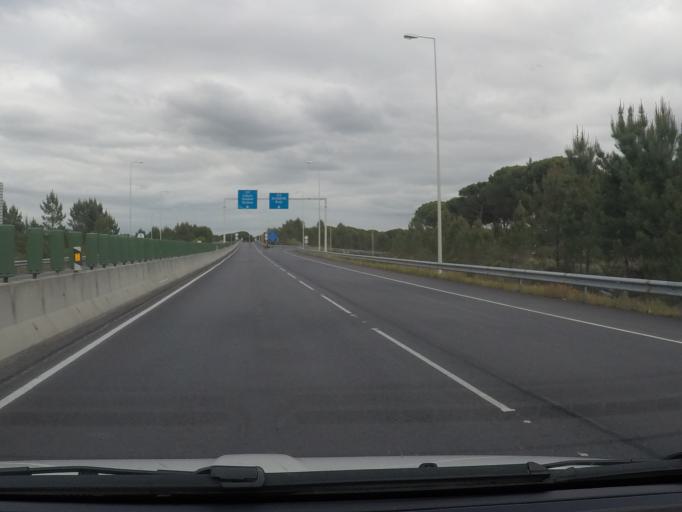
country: PT
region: Setubal
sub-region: Grandola
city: Grandola
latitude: 38.2237
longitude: -8.5223
